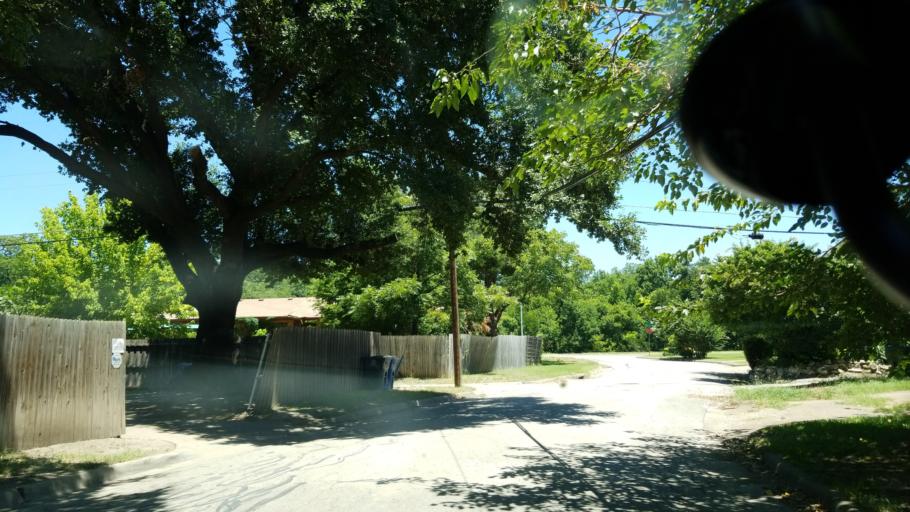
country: US
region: Texas
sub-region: Dallas County
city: Cockrell Hill
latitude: 32.6934
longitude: -96.8360
